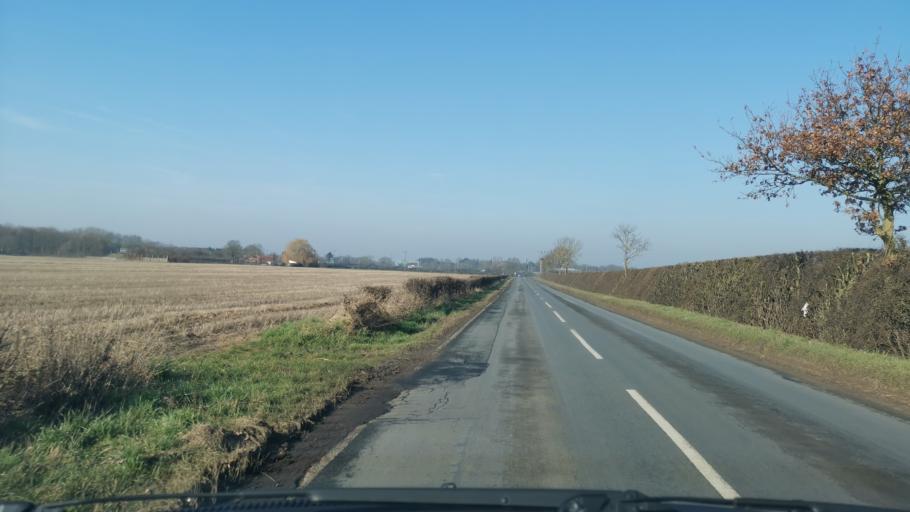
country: GB
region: England
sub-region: City of York
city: Murton
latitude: 53.9849
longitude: -1.0140
